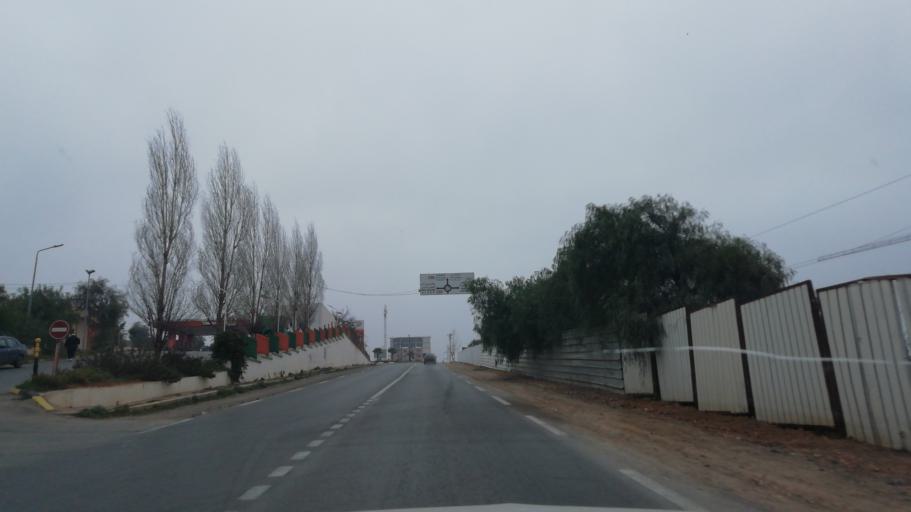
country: DZ
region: Mascara
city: Mascara
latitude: 35.4148
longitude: 0.1434
